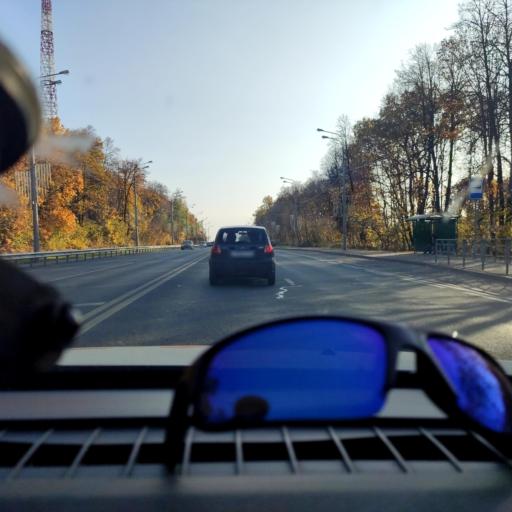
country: RU
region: Samara
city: Samara
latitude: 53.2954
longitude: 50.2252
